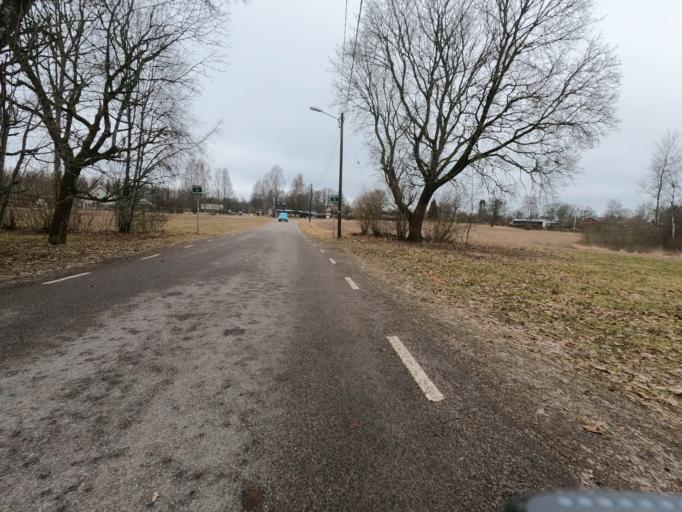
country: SE
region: Kronoberg
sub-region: Ljungby Kommun
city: Ljungby
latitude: 56.8274
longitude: 13.7561
